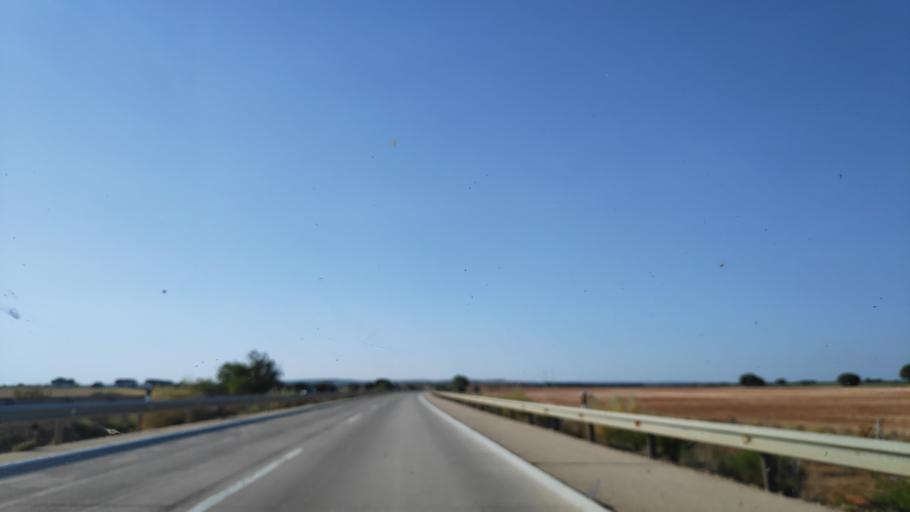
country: ES
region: Castille-La Mancha
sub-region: Provincia de Cuenca
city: Casas de Guijarro
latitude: 39.3091
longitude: -2.2028
